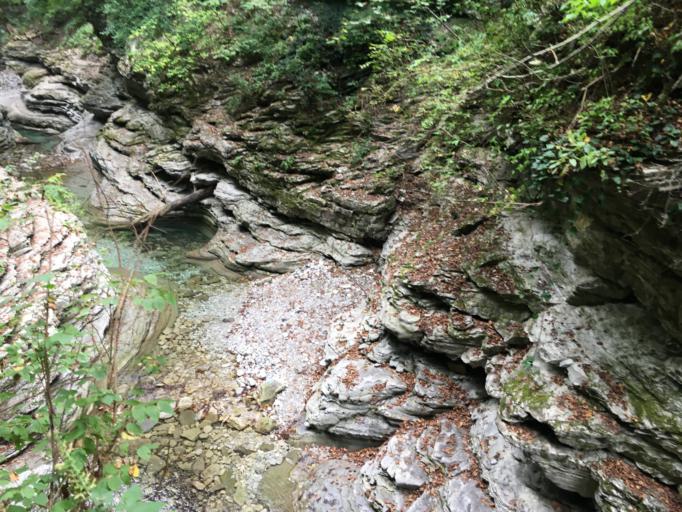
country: RU
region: Krasnodarskiy
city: Tuapse
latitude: 44.2626
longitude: 39.2068
